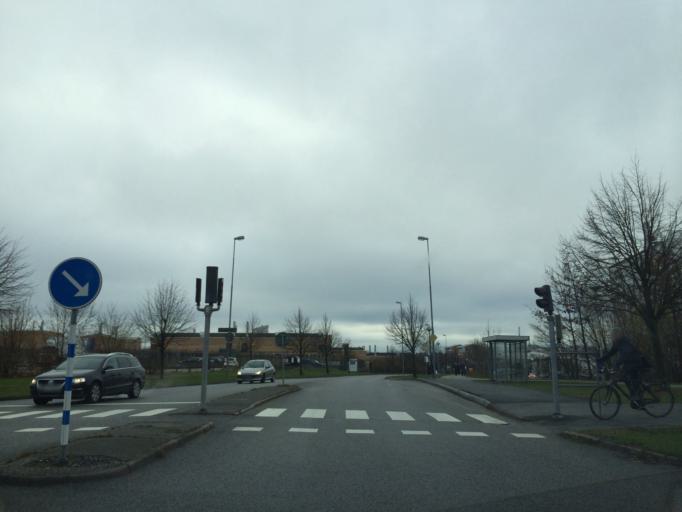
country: SE
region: Skane
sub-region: Lunds Kommun
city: Lund
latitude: 55.7157
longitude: 13.2172
